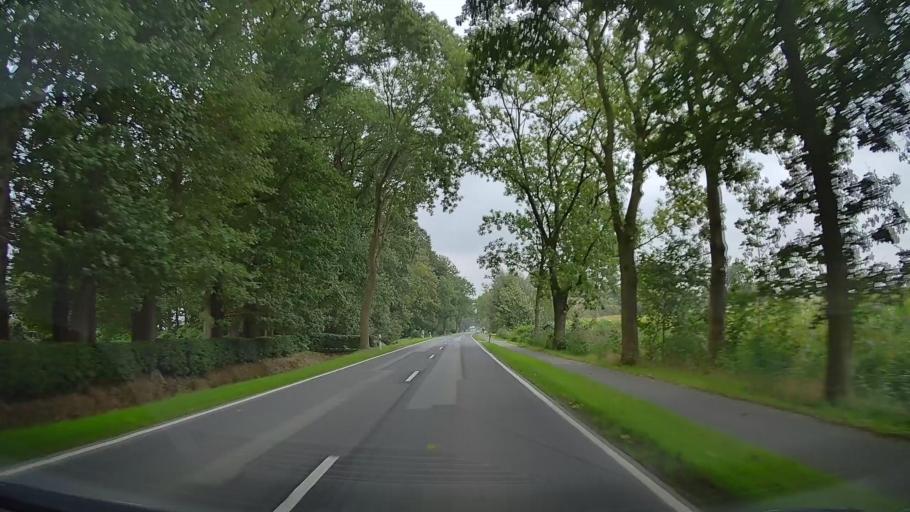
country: DE
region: Lower Saxony
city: Geversdorf
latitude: 53.8177
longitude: 9.1024
